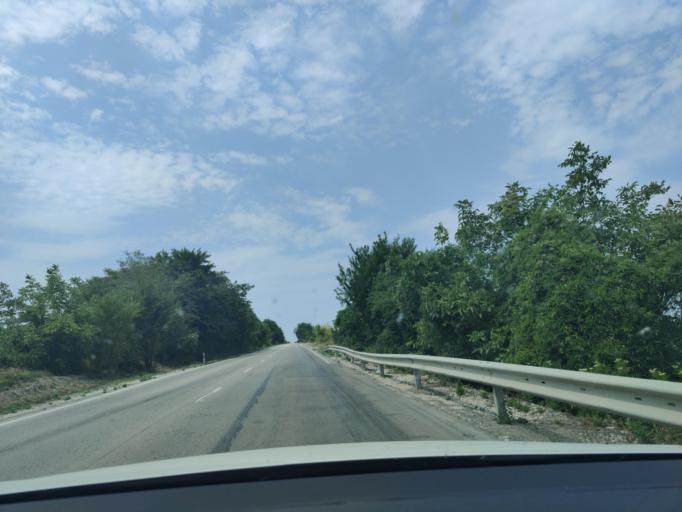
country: BG
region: Vidin
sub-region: Obshtina Vidin
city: Dunavtsi
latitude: 43.8966
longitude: 22.8067
